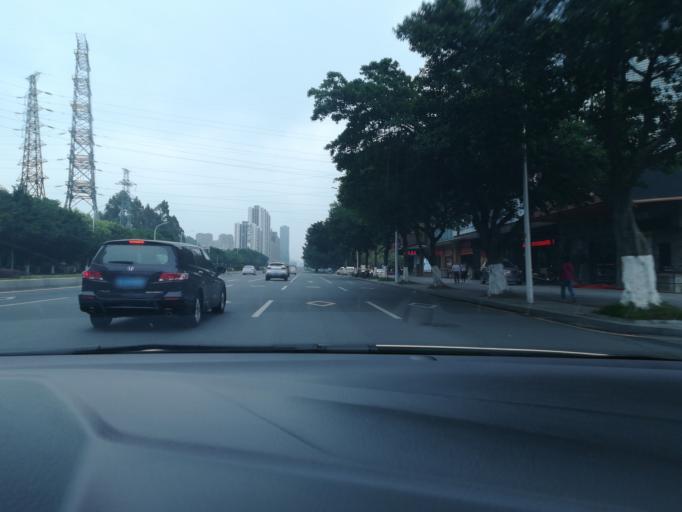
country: CN
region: Guangdong
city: Nansha
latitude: 22.8006
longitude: 113.5570
